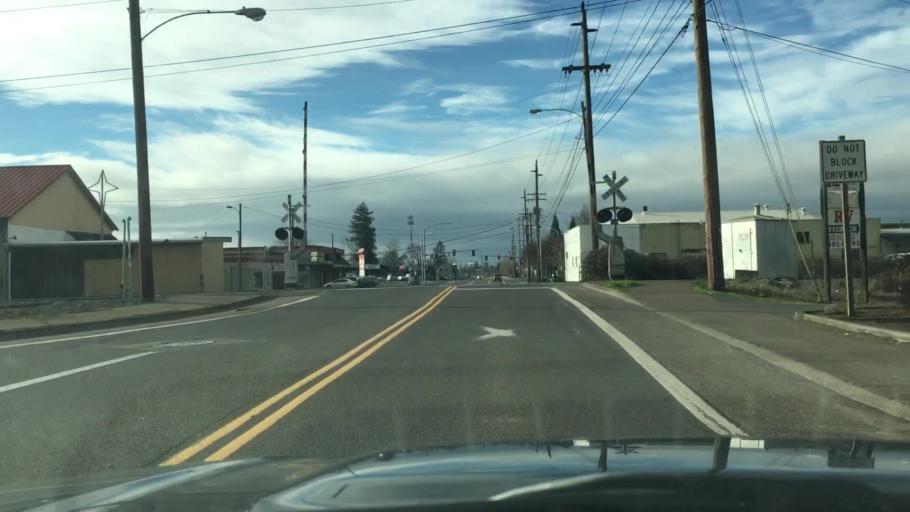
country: US
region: Oregon
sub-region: Lane County
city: Eugene
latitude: 44.0637
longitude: -123.1341
